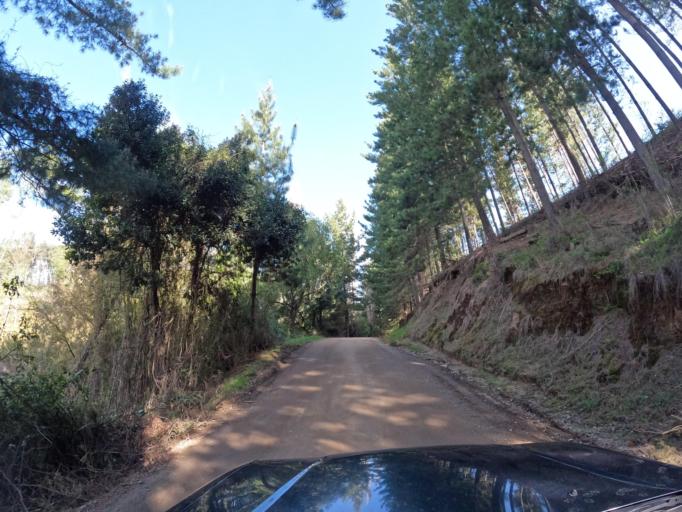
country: CL
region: Biobio
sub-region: Provincia de Biobio
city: La Laja
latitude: -37.0779
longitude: -72.8359
